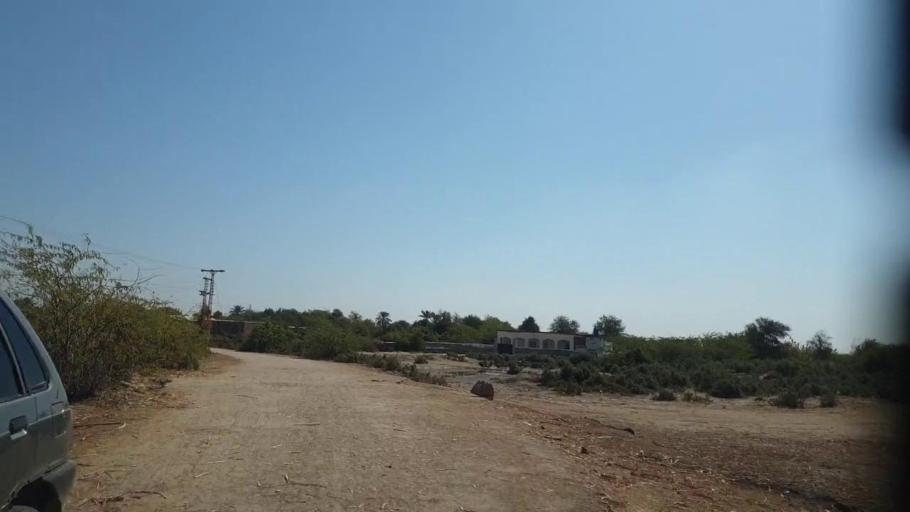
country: PK
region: Sindh
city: Mirpur Khas
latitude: 25.5825
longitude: 69.1127
